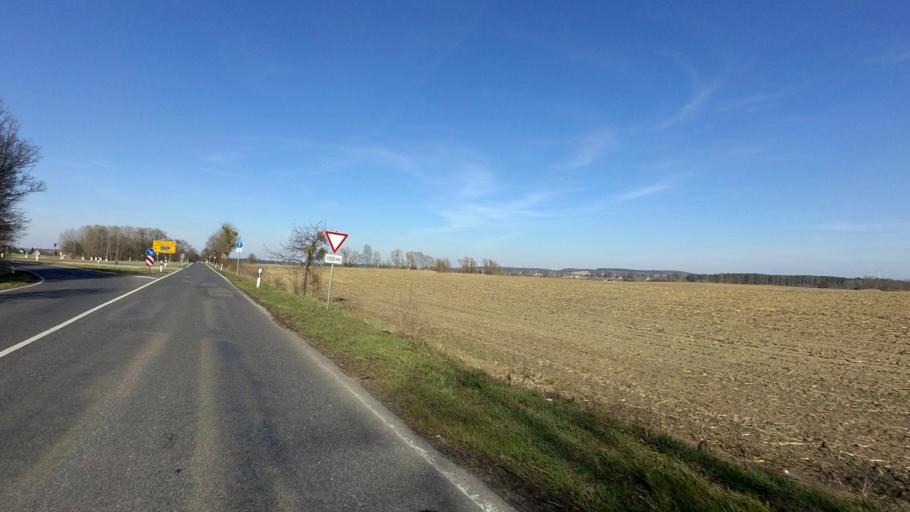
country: DE
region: Brandenburg
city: Angermunde
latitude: 52.9696
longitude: 13.9650
